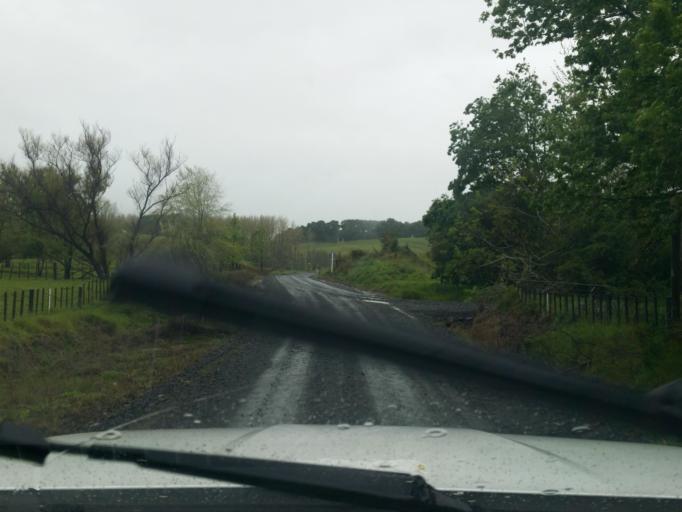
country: NZ
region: Northland
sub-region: Whangarei
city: Maungatapere
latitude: -35.8129
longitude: 174.0368
